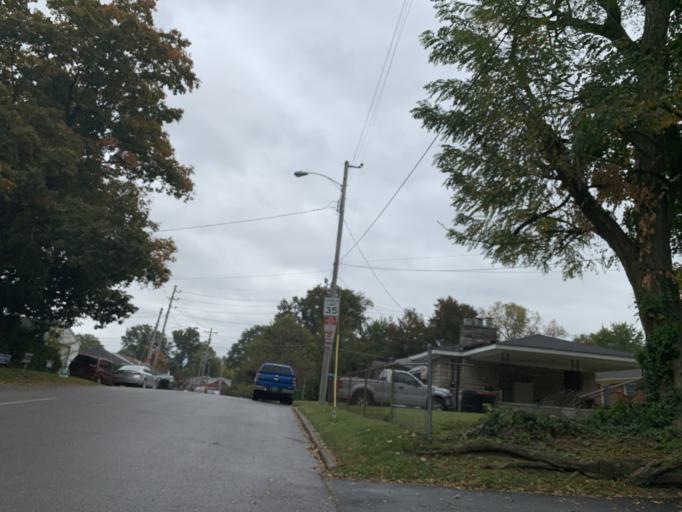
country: US
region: Indiana
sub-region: Floyd County
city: New Albany
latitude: 38.2719
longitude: -85.8179
